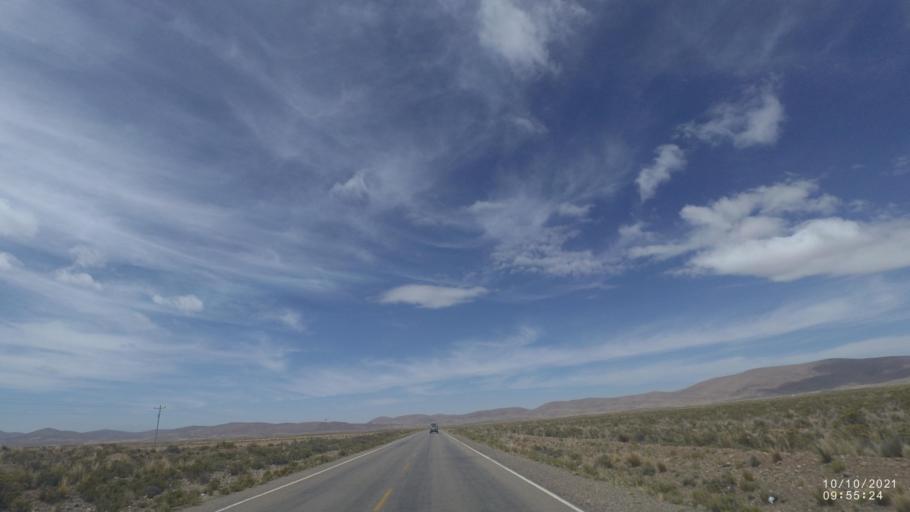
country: BO
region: La Paz
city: Colquiri
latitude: -17.3076
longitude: -67.3660
